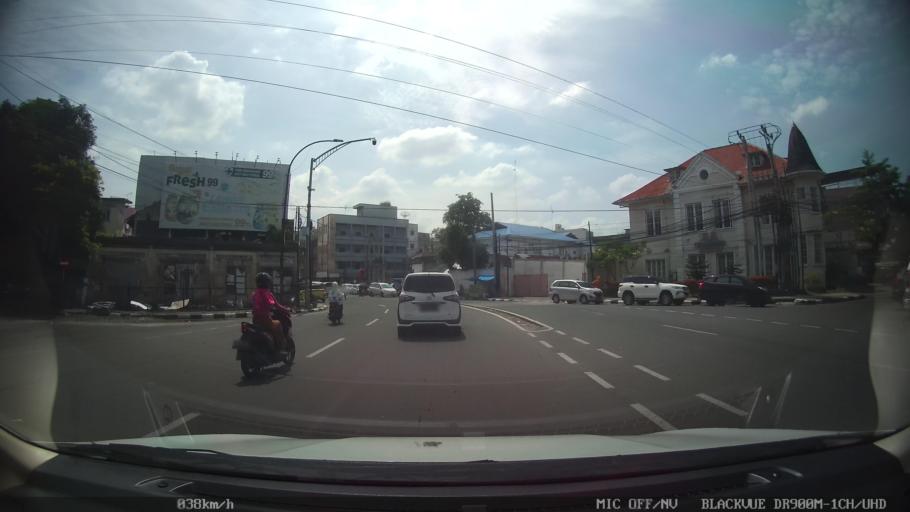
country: ID
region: North Sumatra
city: Medan
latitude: 3.5841
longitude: 98.6782
